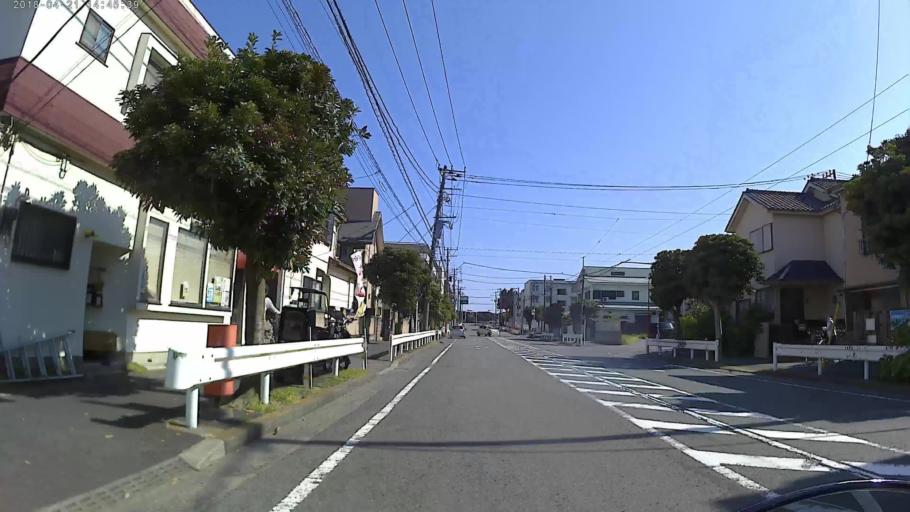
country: JP
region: Kanagawa
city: Hiratsuka
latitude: 35.3180
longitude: 139.3476
